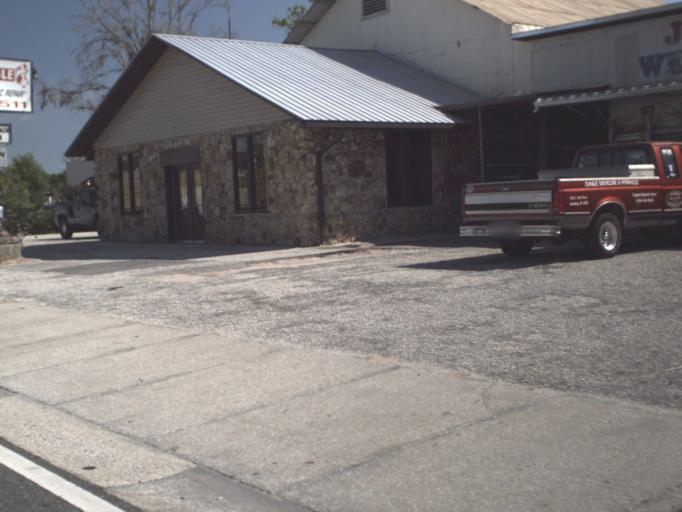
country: US
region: Florida
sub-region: Lake County
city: Leesburg
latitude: 28.8000
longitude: -81.8876
